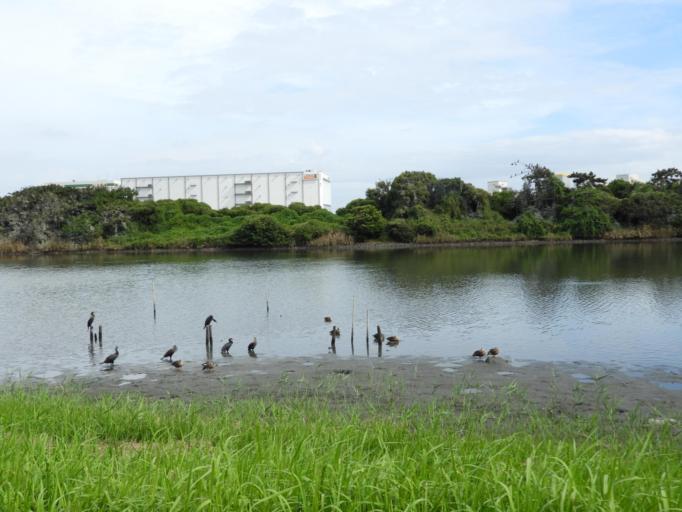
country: JP
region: Kanagawa
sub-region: Kawasaki-shi
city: Kawasaki
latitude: 35.5811
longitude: 139.7650
